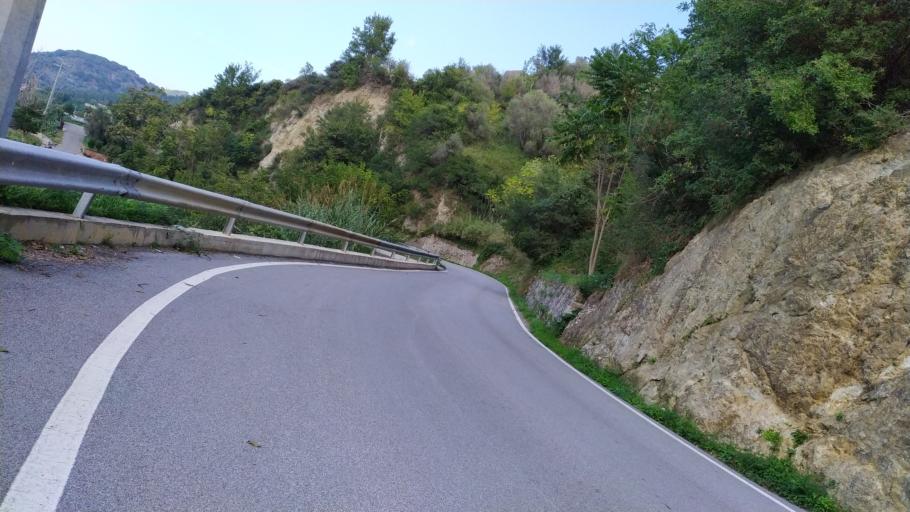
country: IT
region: Sicily
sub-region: Messina
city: Saponara
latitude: 38.1925
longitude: 15.4285
